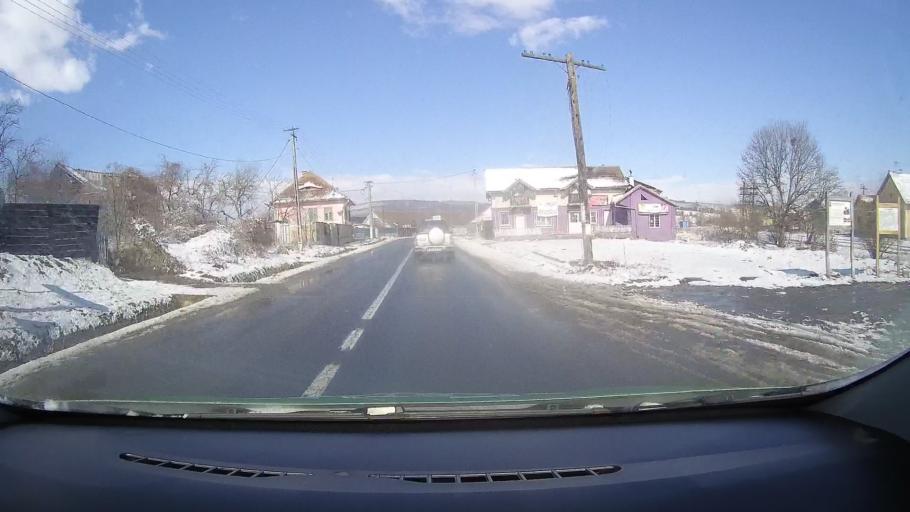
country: RO
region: Sibiu
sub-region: Comuna Rosia
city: Rosia
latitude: 45.8024
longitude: 24.3522
